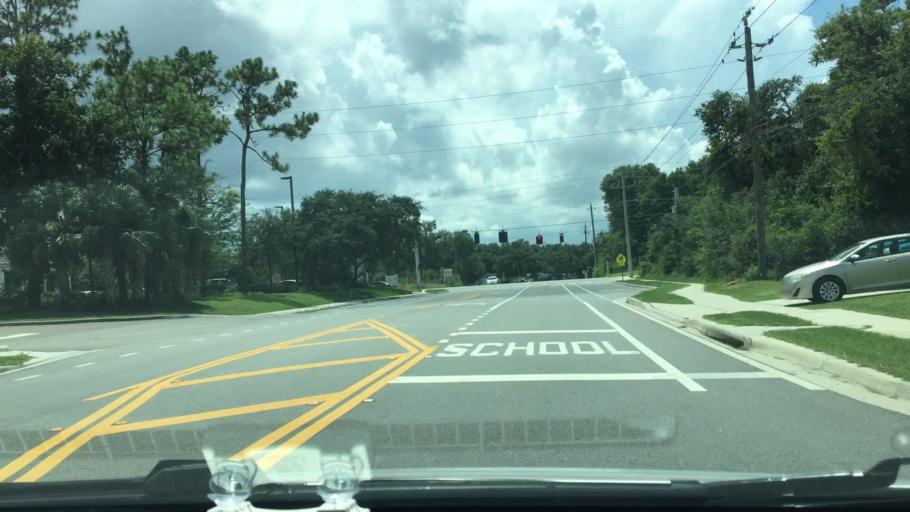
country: US
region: Florida
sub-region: Volusia County
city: Deltona
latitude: 28.8802
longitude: -81.1644
